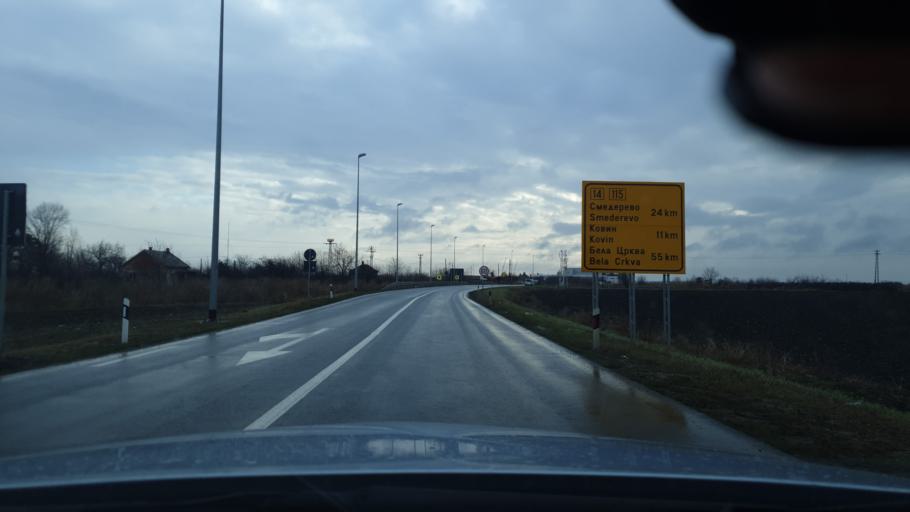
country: RS
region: Autonomna Pokrajina Vojvodina
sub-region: Juznobanatski Okrug
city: Kovin
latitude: 44.8100
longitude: 20.8886
